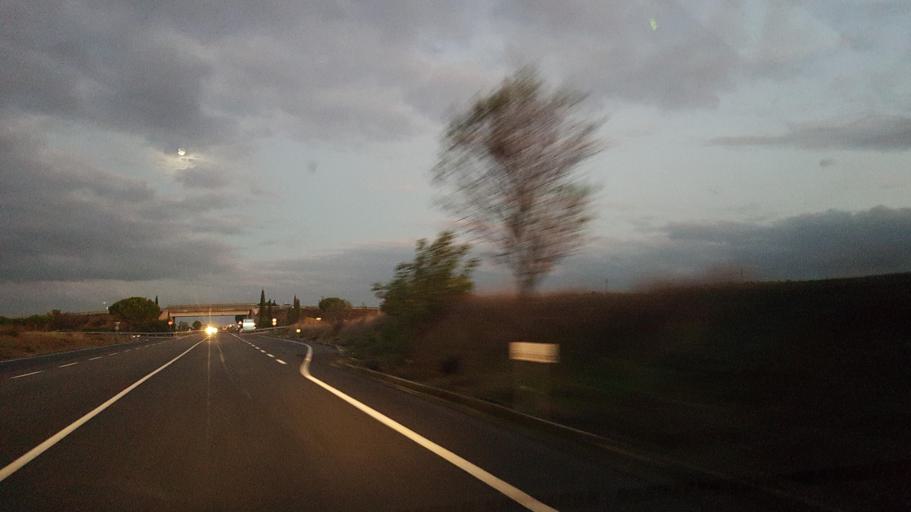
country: IT
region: Apulia
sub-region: Provincia di Taranto
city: Laterza
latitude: 40.6492
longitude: 16.8209
